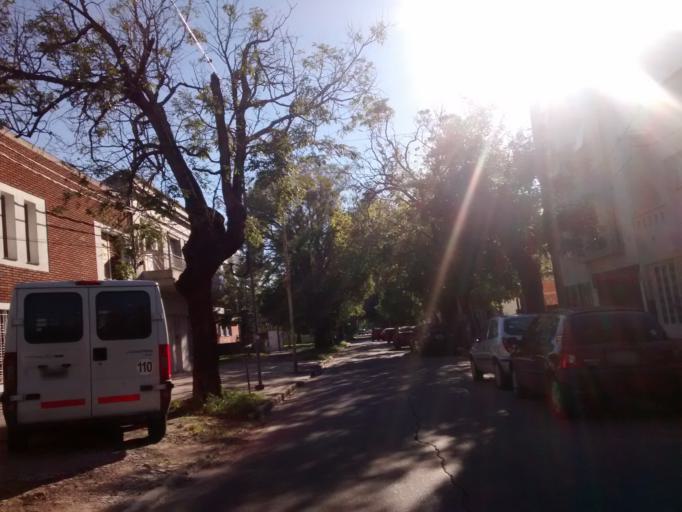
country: AR
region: Buenos Aires
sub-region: Partido de La Plata
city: La Plata
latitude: -34.9325
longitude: -57.9482
